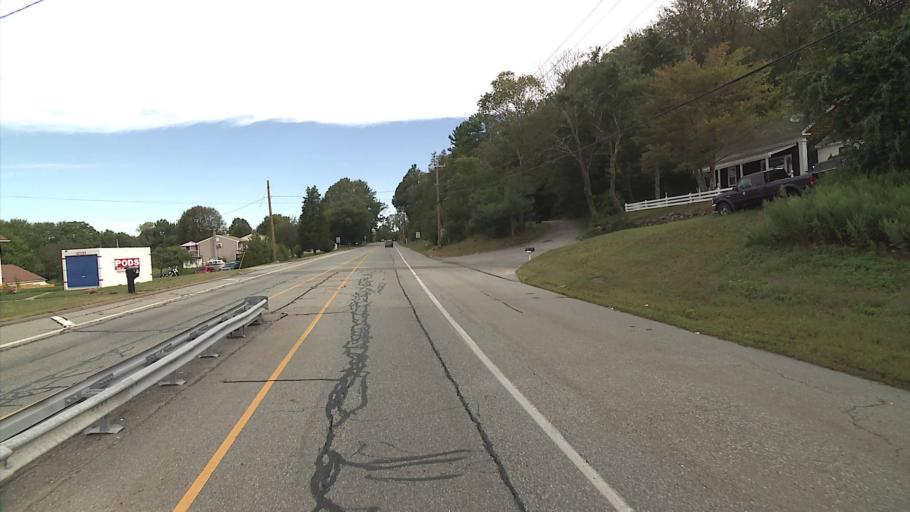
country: US
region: Connecticut
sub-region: New London County
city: Uncasville
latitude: 41.4191
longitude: -72.1102
